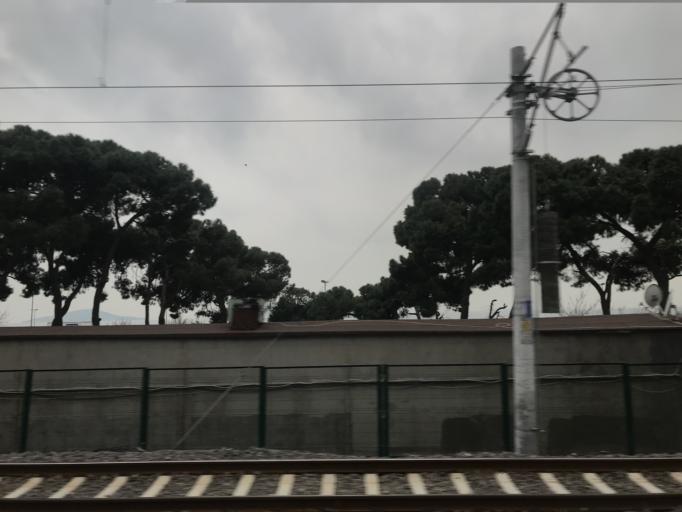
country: TR
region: Istanbul
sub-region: Atasehir
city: Atasehir
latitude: 40.9471
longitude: 29.1024
